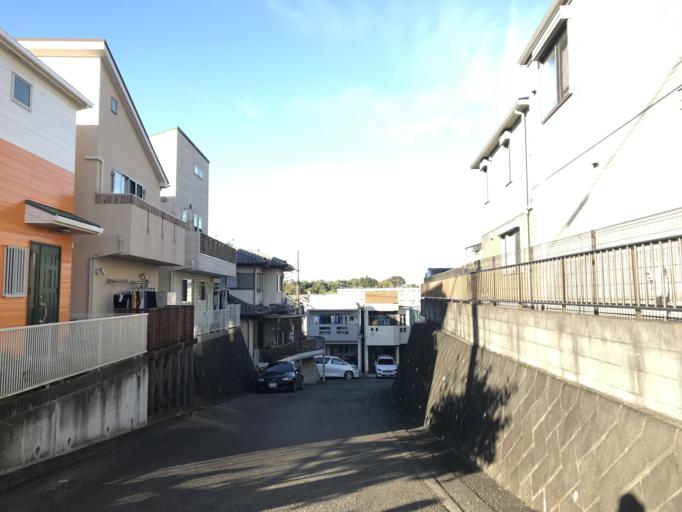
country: JP
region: Kanagawa
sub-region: Kawasaki-shi
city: Kawasaki
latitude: 35.5620
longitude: 139.6229
